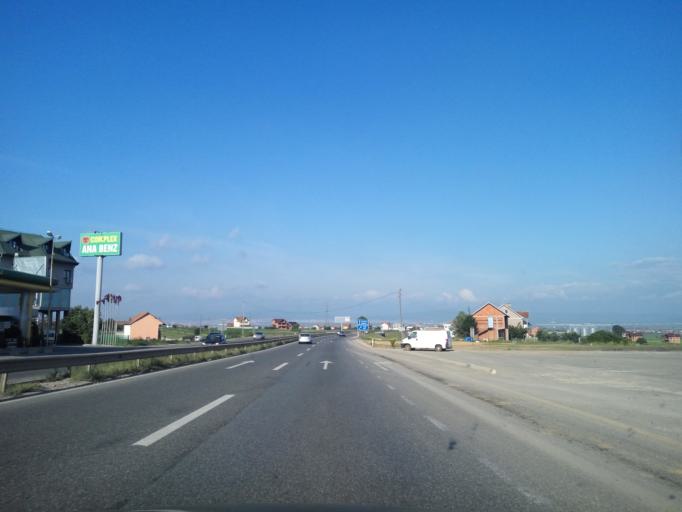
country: XK
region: Pristina
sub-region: Komuna e Gracanices
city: Glanica
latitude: 42.5979
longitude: 21.0055
